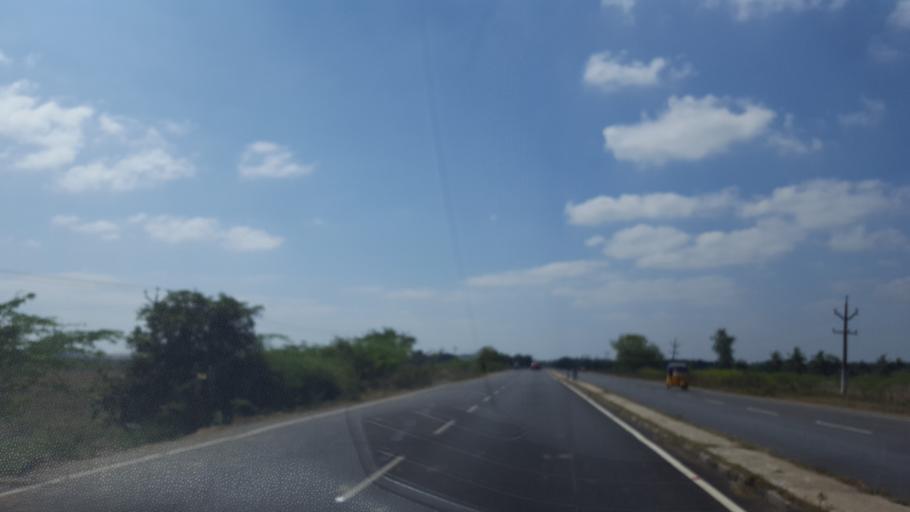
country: IN
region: Tamil Nadu
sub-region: Kancheepuram
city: Mamallapuram
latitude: 12.6635
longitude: 80.1776
